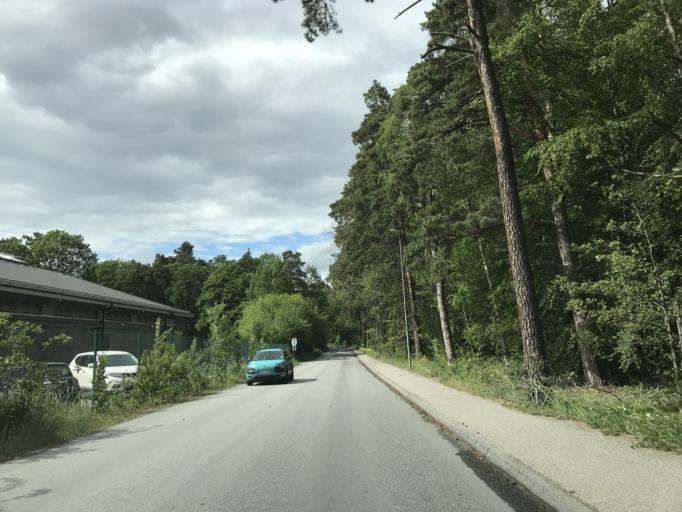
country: SE
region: Stockholm
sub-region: Solna Kommun
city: Solna
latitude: 59.3839
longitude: 18.0092
